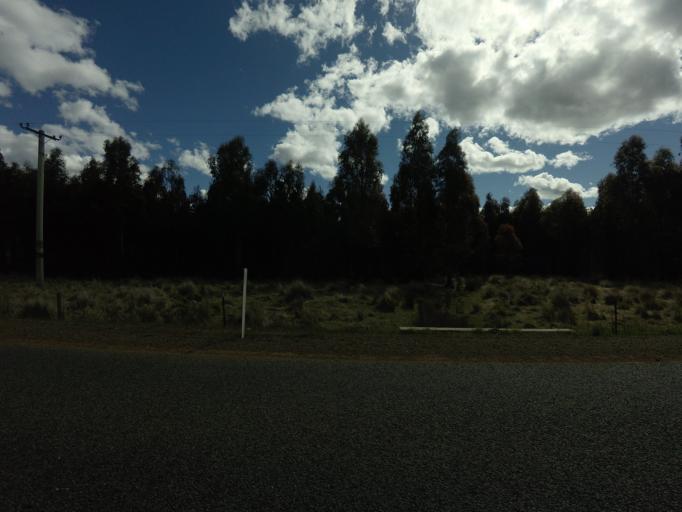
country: AU
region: Tasmania
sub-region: Brighton
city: Bridgewater
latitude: -42.4726
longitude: 147.3223
